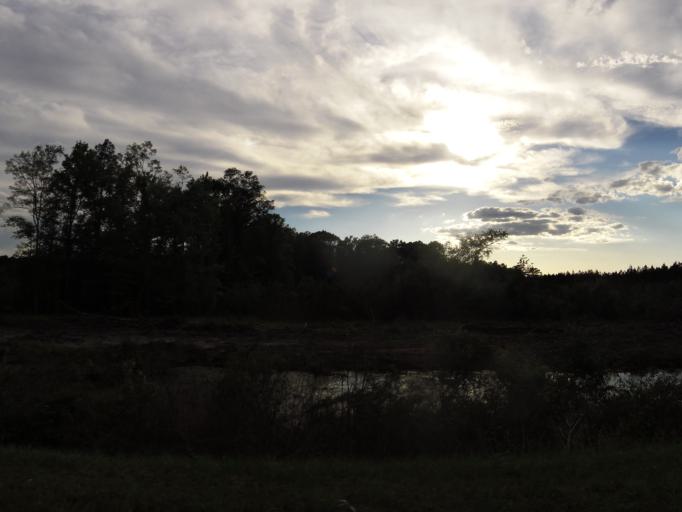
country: US
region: South Carolina
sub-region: Jasper County
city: Hardeeville
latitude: 32.4065
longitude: -81.1003
